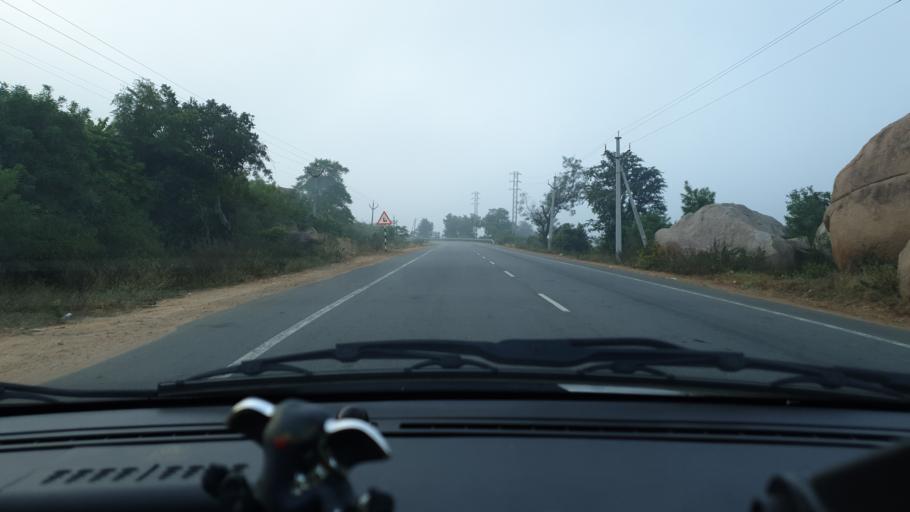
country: IN
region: Telangana
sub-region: Mahbubnagar
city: Farrukhnagar
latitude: 16.8965
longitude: 78.5300
